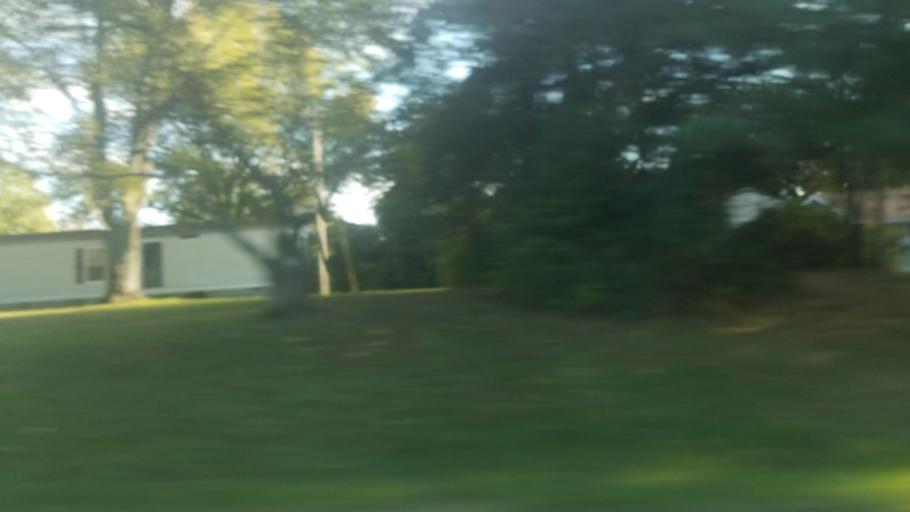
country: US
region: Illinois
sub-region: Williamson County
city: Marion
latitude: 37.7610
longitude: -88.7931
